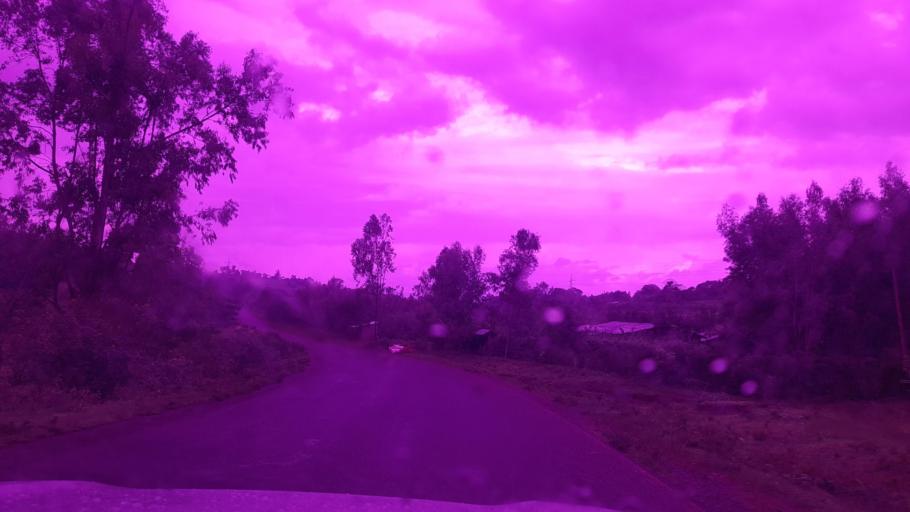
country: ET
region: Oromiya
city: Jima
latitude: 7.7087
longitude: 37.0458
